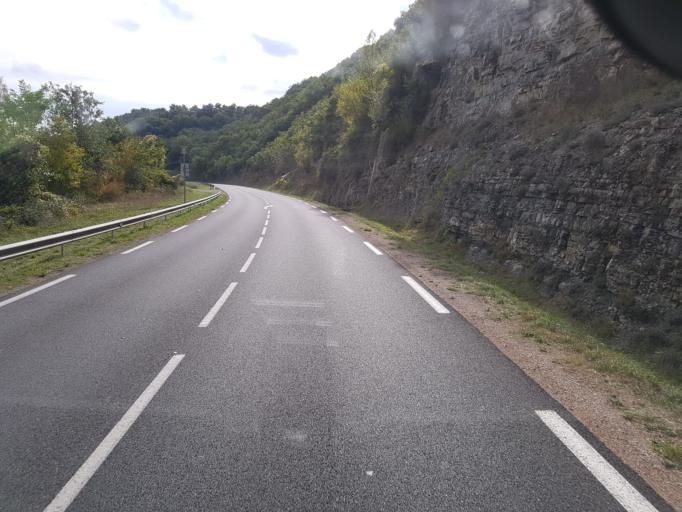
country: FR
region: Midi-Pyrenees
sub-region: Departement de l'Aveyron
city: Saint-Georges-de-Luzencon
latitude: 44.0351
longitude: 2.9618
